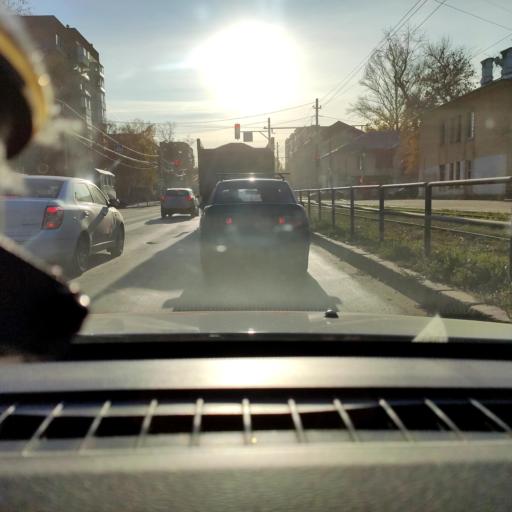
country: RU
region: Samara
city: Samara
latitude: 53.1974
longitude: 50.2215
